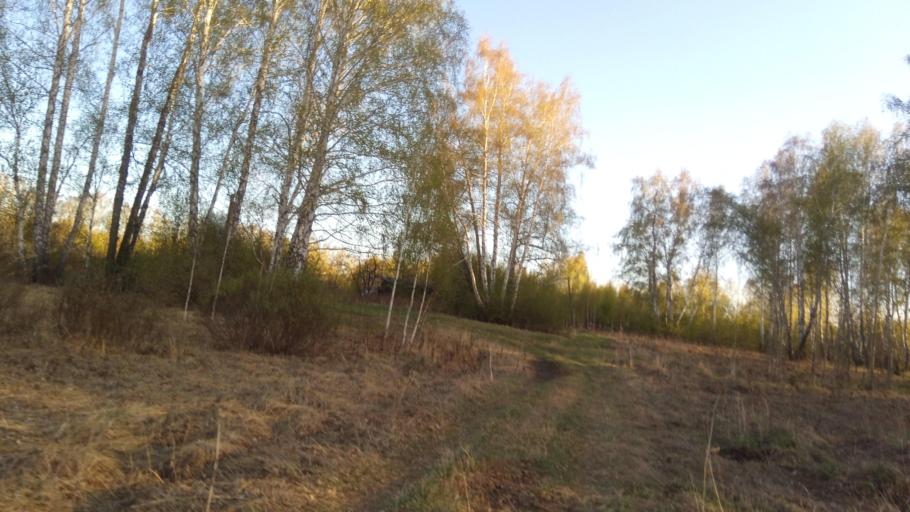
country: RU
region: Chelyabinsk
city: Timiryazevskiy
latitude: 54.9919
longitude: 60.8590
